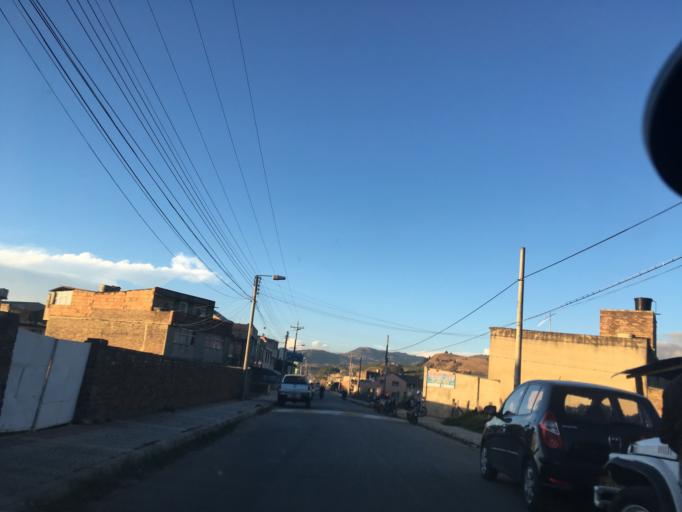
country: CO
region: Boyaca
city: Aquitania
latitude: 5.5213
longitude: -72.8829
